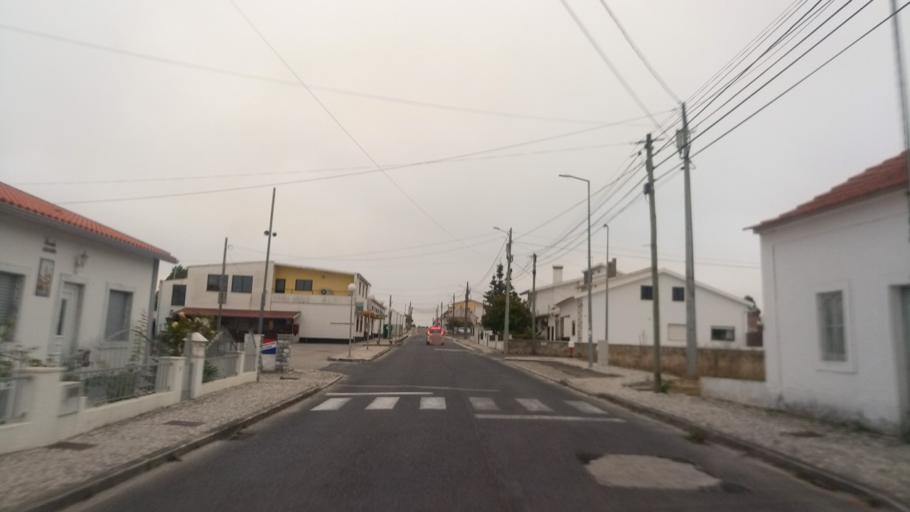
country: PT
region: Leiria
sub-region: Caldas da Rainha
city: Caldas da Rainha
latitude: 39.4329
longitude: -9.1540
